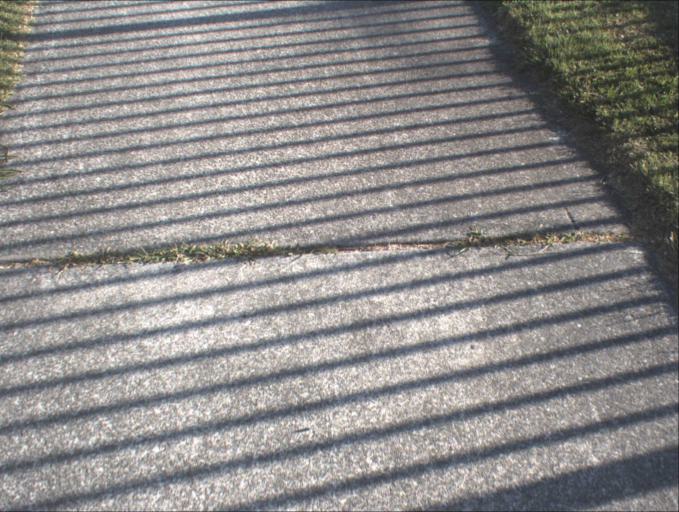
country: AU
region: Queensland
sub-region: Gold Coast
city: Yatala
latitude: -27.7088
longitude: 153.2202
